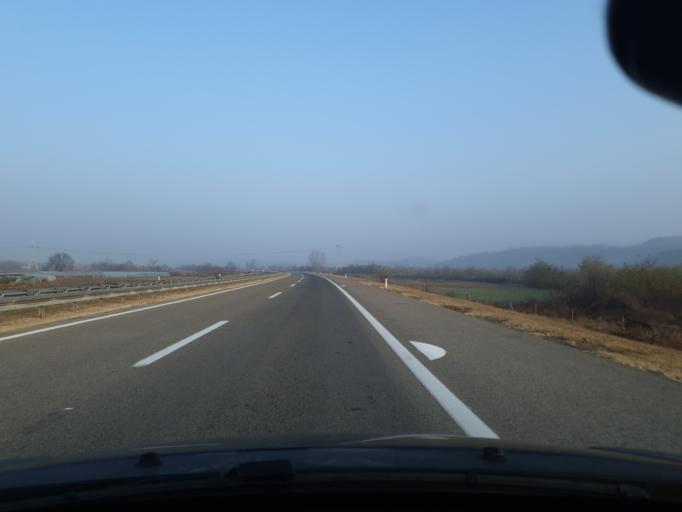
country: RS
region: Central Serbia
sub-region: Jablanicki Okrug
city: Leskovac
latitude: 43.0060
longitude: 22.0249
